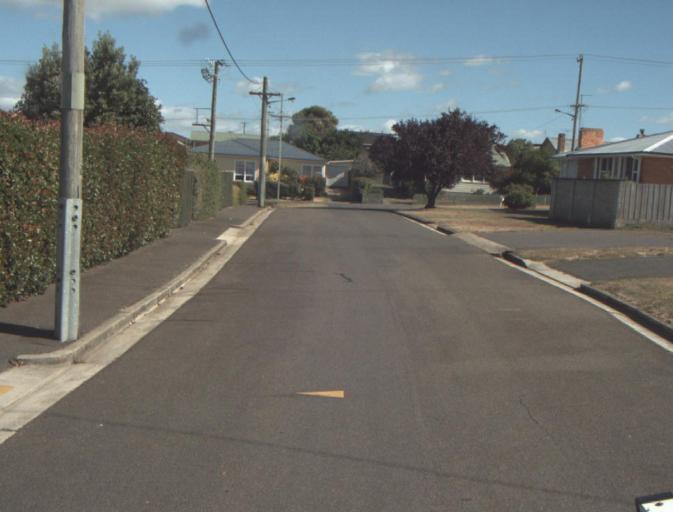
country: AU
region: Tasmania
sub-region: Launceston
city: Newstead
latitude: -41.4252
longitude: 147.1765
